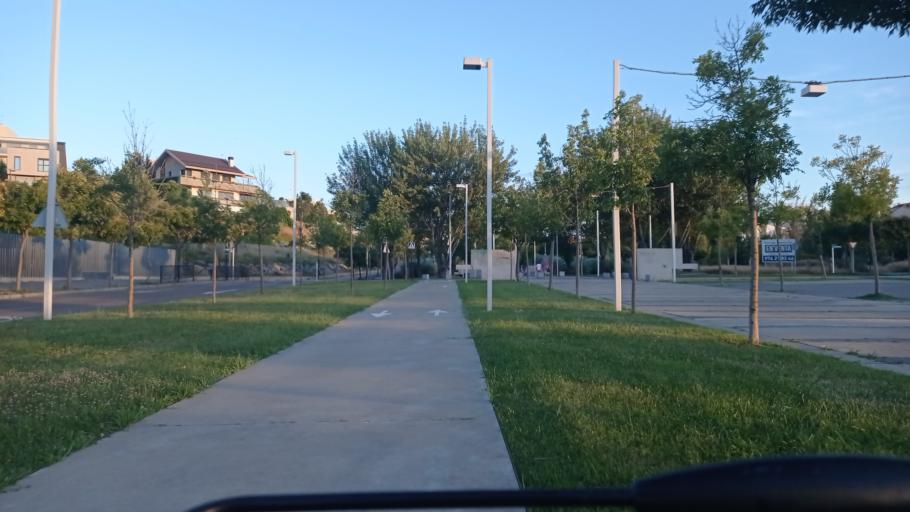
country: ES
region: Aragon
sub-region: Provincia de Zaragoza
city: Oliver-Valdefierro, Oliver, Valdefierro
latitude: 41.6568
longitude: -0.9247
